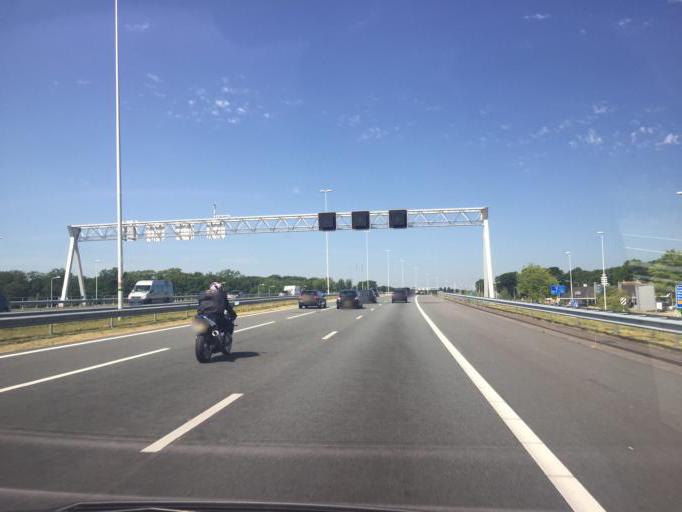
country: NL
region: Utrecht
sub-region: Gemeente Utrechtse Heuvelrug
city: Maarsbergen
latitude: 52.0540
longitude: 5.4066
